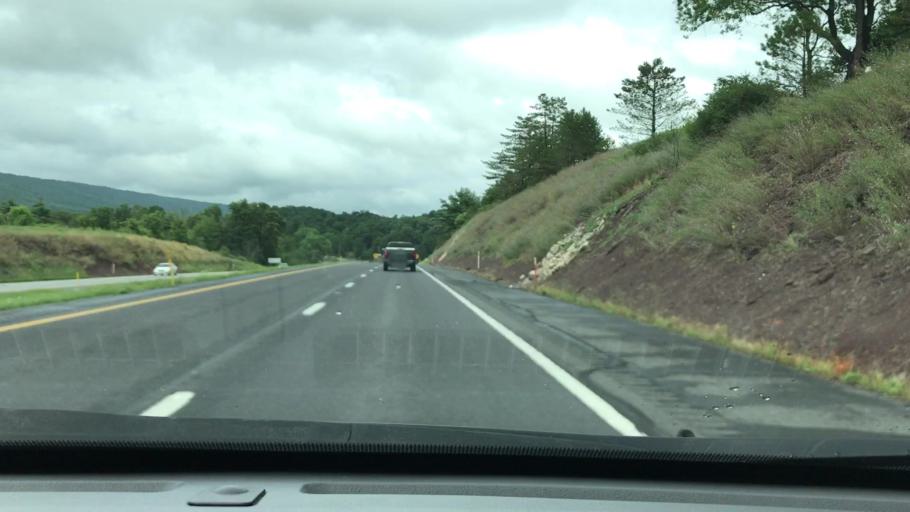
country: US
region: Pennsylvania
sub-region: Bedford County
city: Earlston
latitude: 39.9363
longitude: -78.2292
